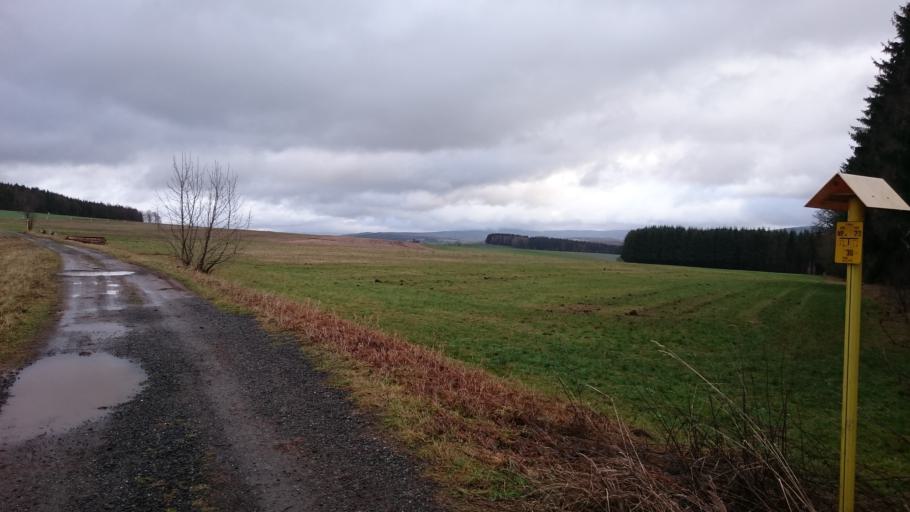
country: DE
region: Saxony
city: Schneeberg
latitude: 50.6074
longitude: 12.5968
